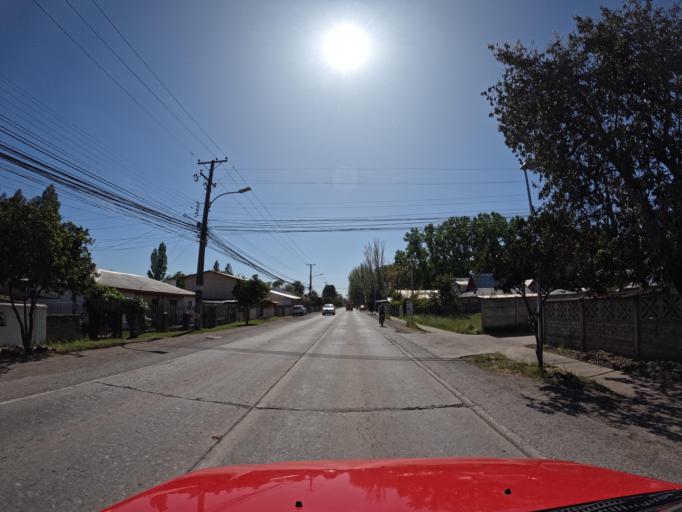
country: CL
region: Maule
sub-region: Provincia de Curico
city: Molina
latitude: -35.0588
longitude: -71.2665
